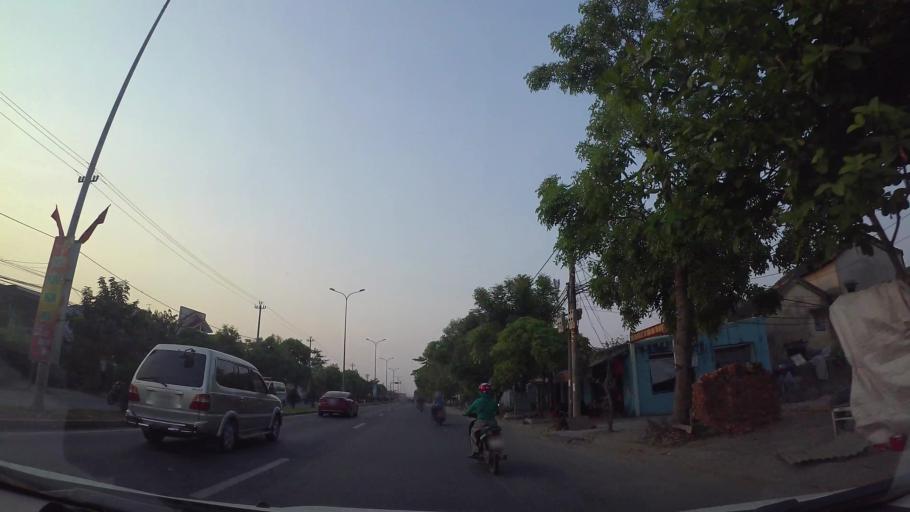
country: VN
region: Da Nang
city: Cam Le
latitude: 15.9576
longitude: 108.2155
